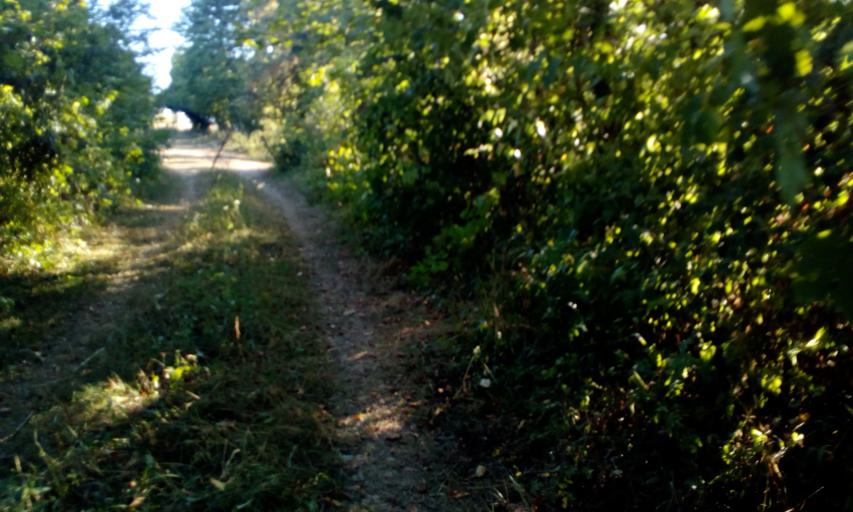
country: FR
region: Lorraine
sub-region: Departement de Meurthe-et-Moselle
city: Pagny-sur-Moselle
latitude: 48.9666
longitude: 5.8819
